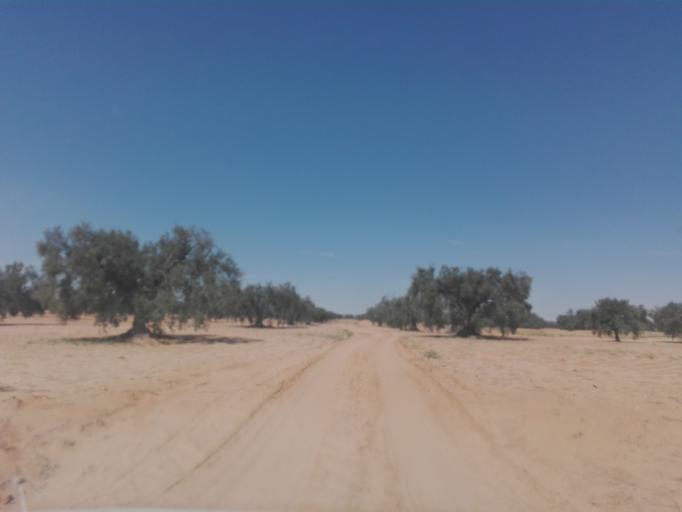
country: TN
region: Safaqis
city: Bi'r `Ali Bin Khalifah
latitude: 34.6625
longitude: 10.3144
